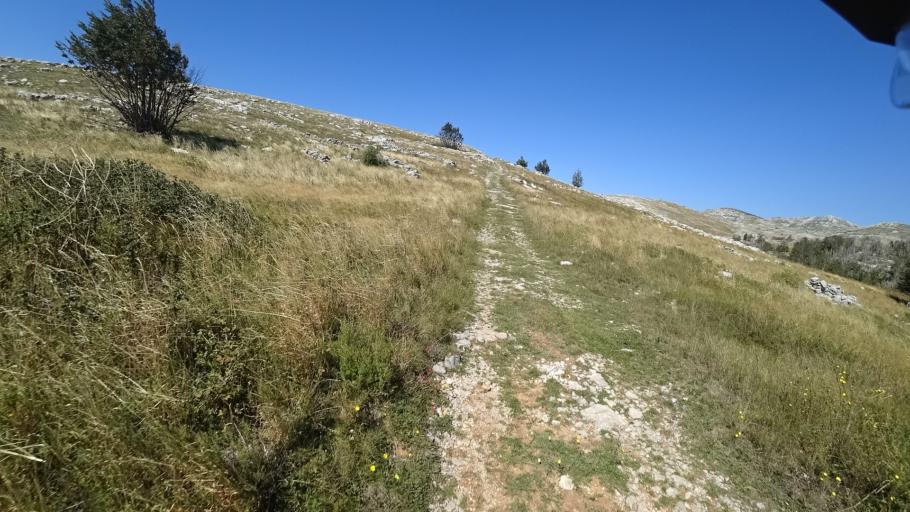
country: HR
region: Splitsko-Dalmatinska
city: Hrvace
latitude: 43.9149
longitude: 16.6097
